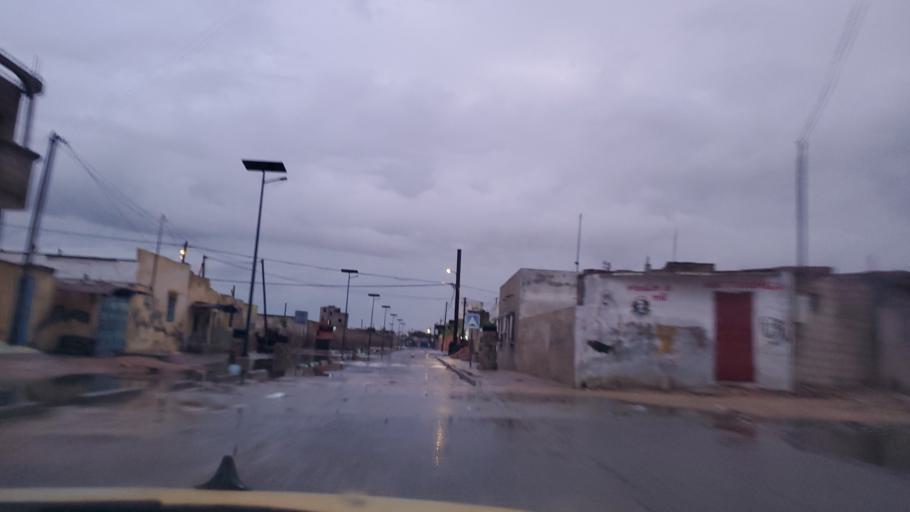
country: SN
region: Saint-Louis
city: Saint-Louis
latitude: 16.0121
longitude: -16.4930
